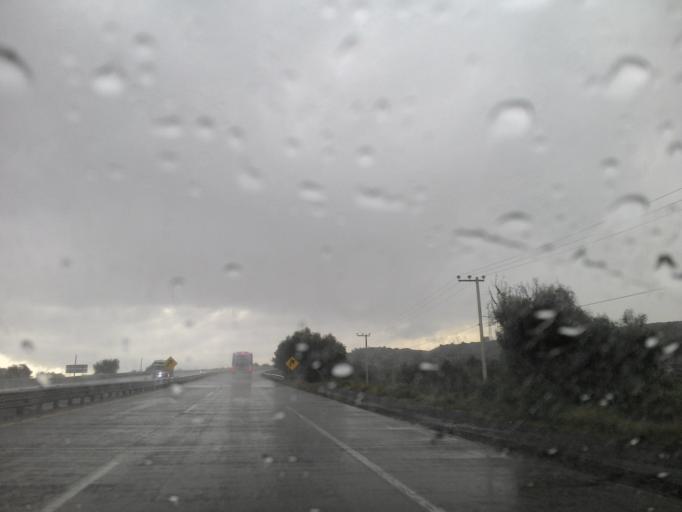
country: MX
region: Hidalgo
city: Zempoala
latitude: 19.8827
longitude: -98.6572
